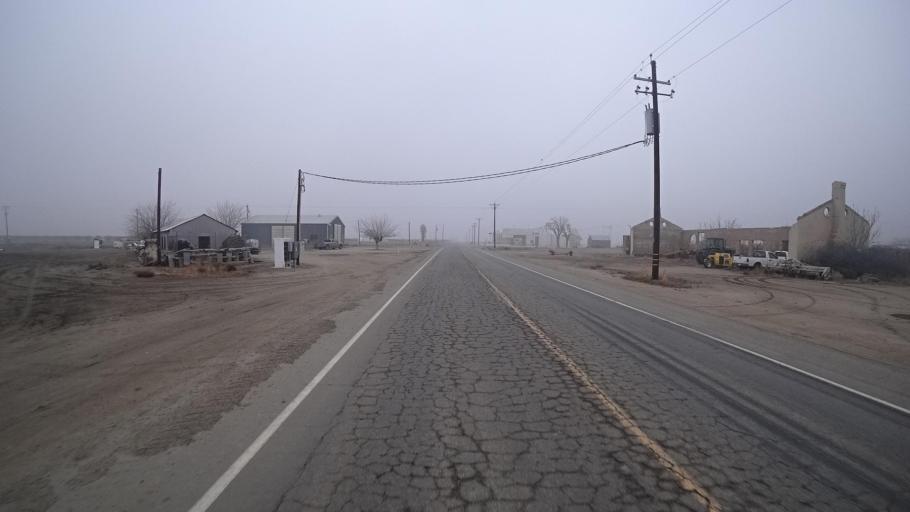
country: US
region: California
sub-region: Kern County
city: Buttonwillow
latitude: 35.4262
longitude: -119.5187
